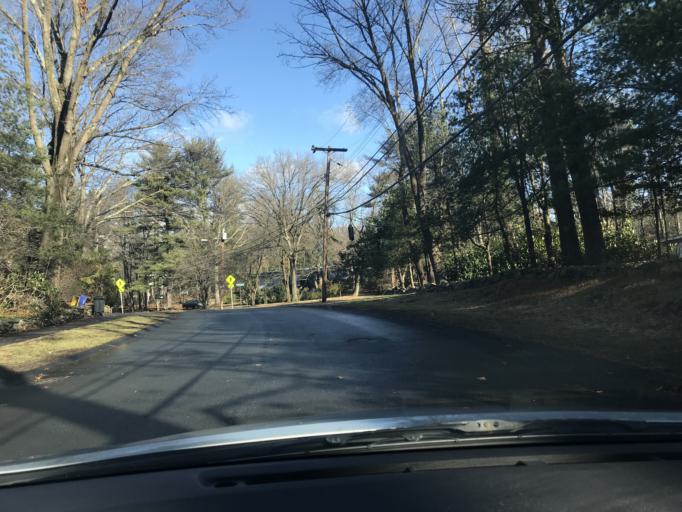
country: US
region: Massachusetts
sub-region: Middlesex County
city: Lexington
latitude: 42.4750
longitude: -71.2309
